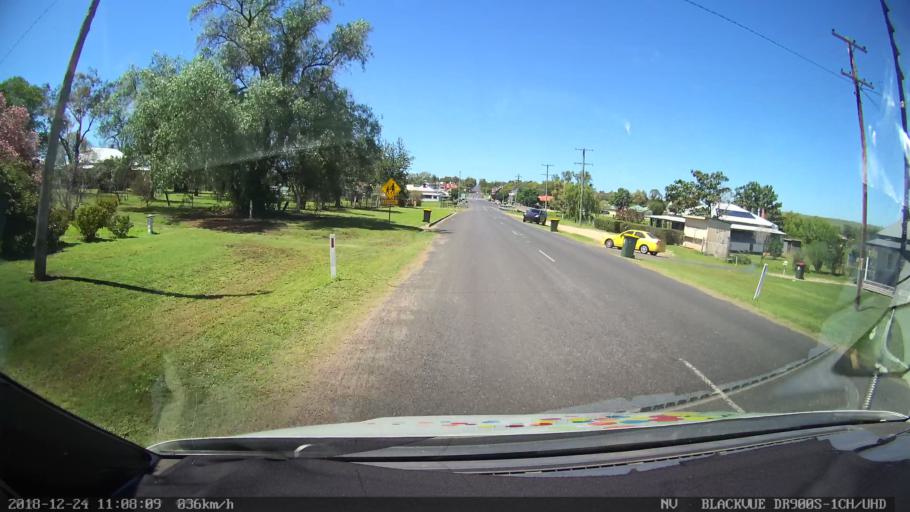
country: AU
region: New South Wales
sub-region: Upper Hunter Shire
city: Merriwa
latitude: -32.1360
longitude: 150.3564
